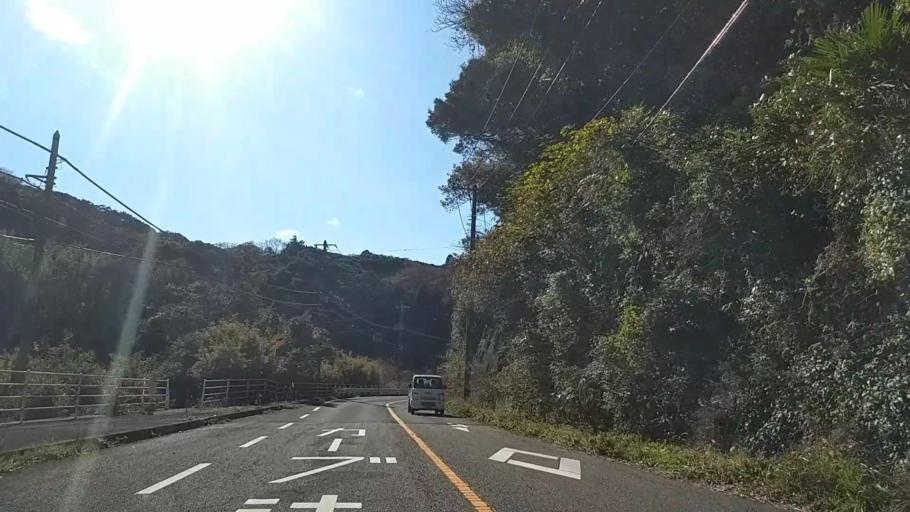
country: JP
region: Chiba
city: Tateyama
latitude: 34.9582
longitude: 139.8514
